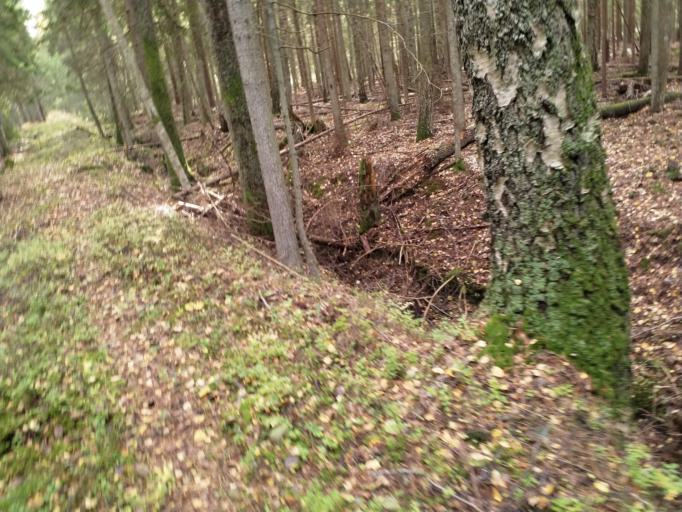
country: LV
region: Dundaga
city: Dundaga
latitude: 57.6542
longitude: 22.2830
